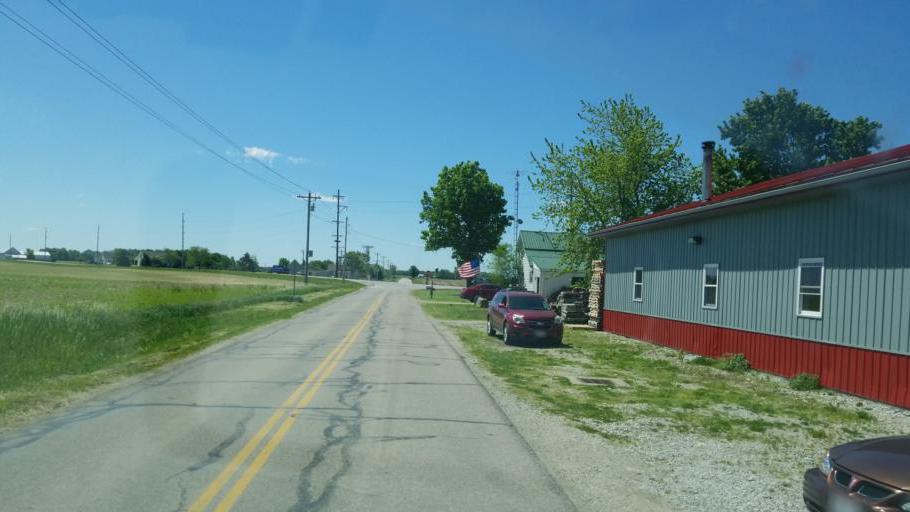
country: US
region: Ohio
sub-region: Shelby County
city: Anna
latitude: 40.3792
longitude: -84.2403
